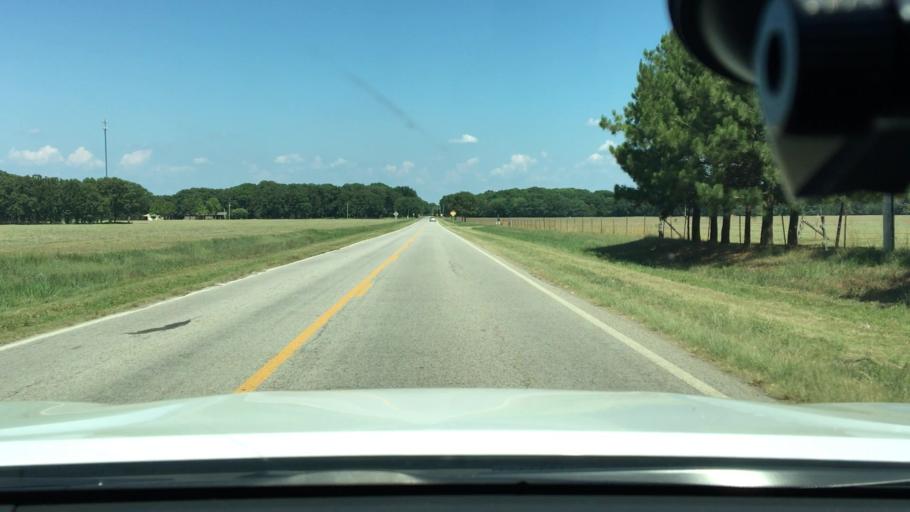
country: US
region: Arkansas
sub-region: Johnson County
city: Coal Hill
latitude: 35.3576
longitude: -93.5588
